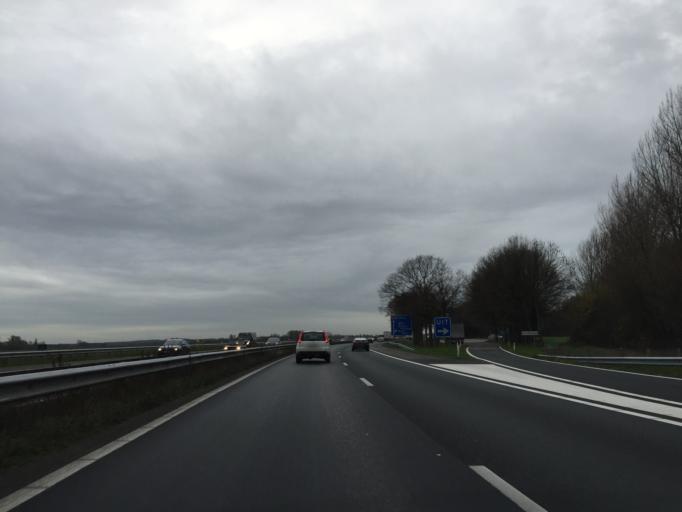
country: NL
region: North Brabant
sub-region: Roosendaal
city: Roosendaal
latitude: 51.5115
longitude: 4.4138
